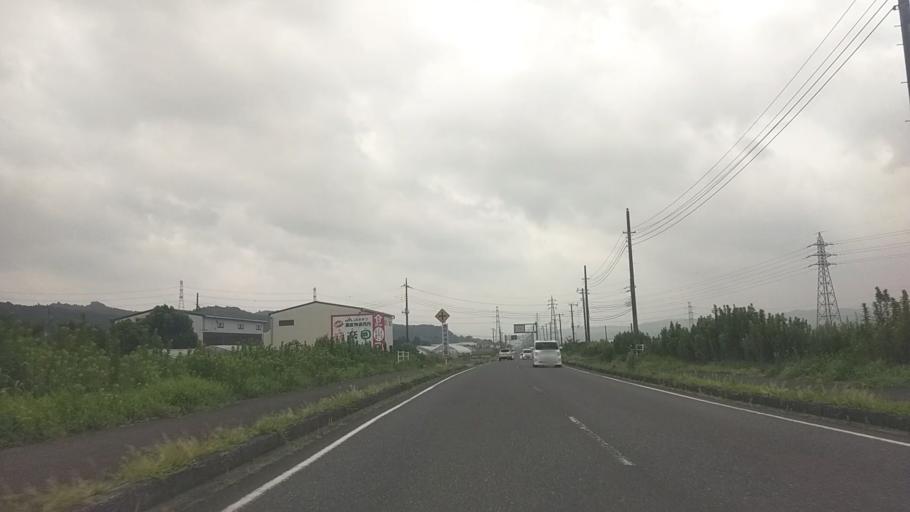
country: JP
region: Chiba
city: Kisarazu
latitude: 35.3547
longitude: 140.0547
